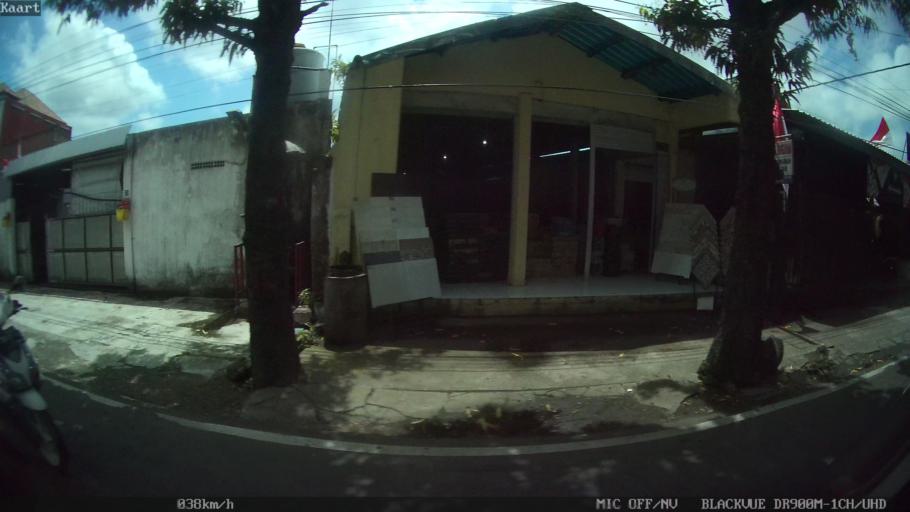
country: ID
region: Bali
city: Banjar Sedang
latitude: -8.5642
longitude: 115.2789
